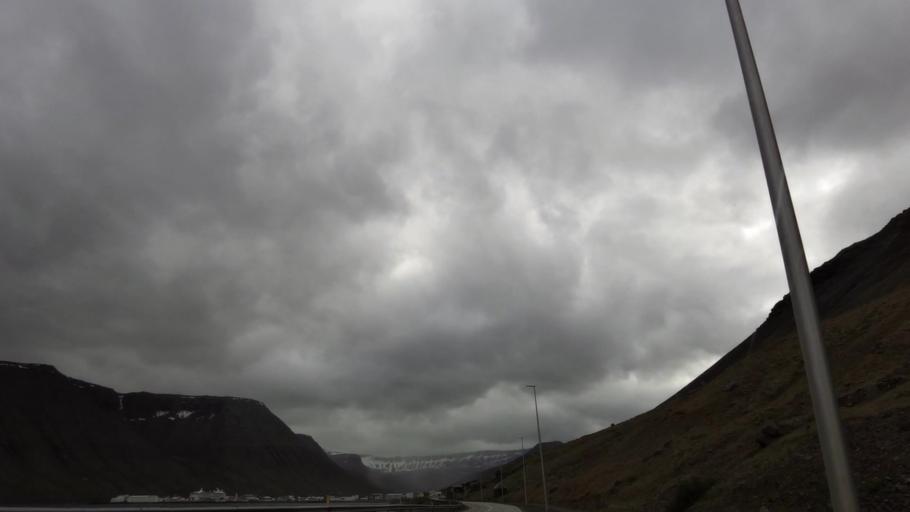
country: IS
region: Westfjords
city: Isafjoerdur
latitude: 66.0878
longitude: -23.1184
